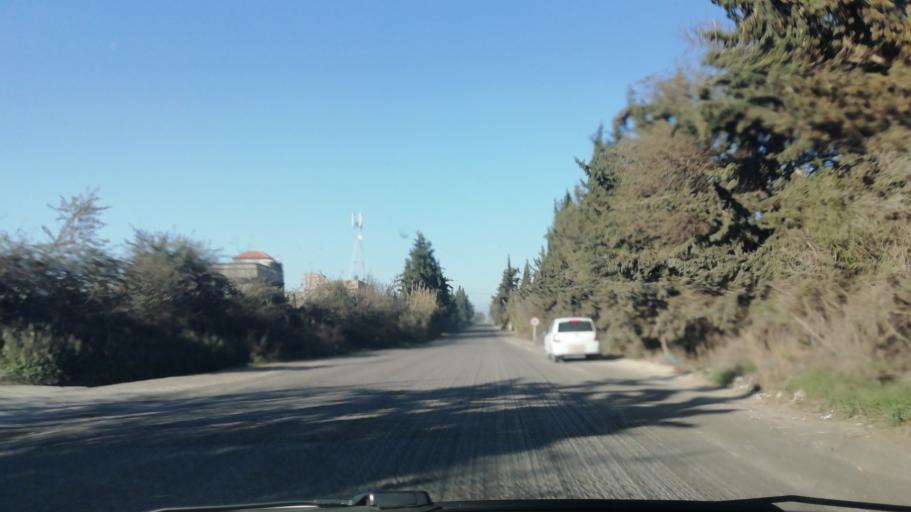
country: DZ
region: Mascara
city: Mascara
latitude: 35.5821
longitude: 0.0283
